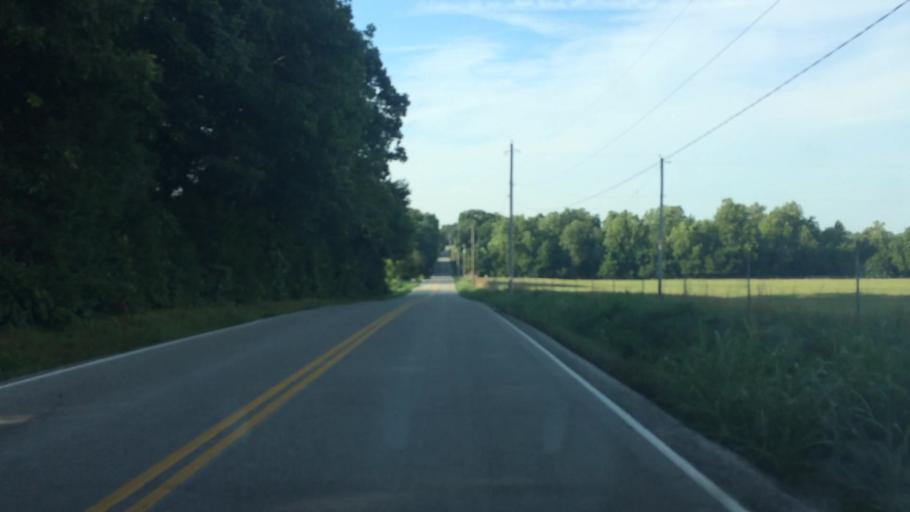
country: US
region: Missouri
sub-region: Greene County
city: Strafford
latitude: 37.2620
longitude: -93.1878
